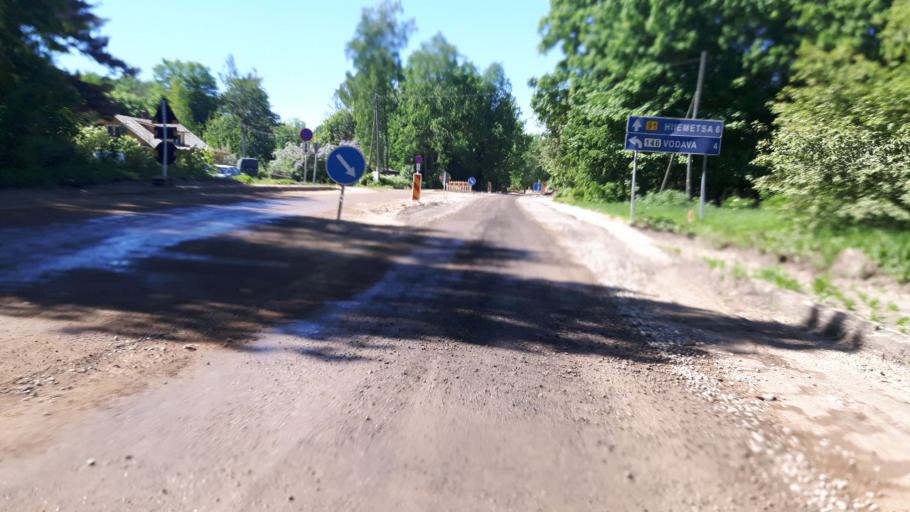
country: EE
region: Ida-Virumaa
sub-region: Narva-Joesuu linn
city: Narva-Joesuu
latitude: 59.4182
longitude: 27.9715
